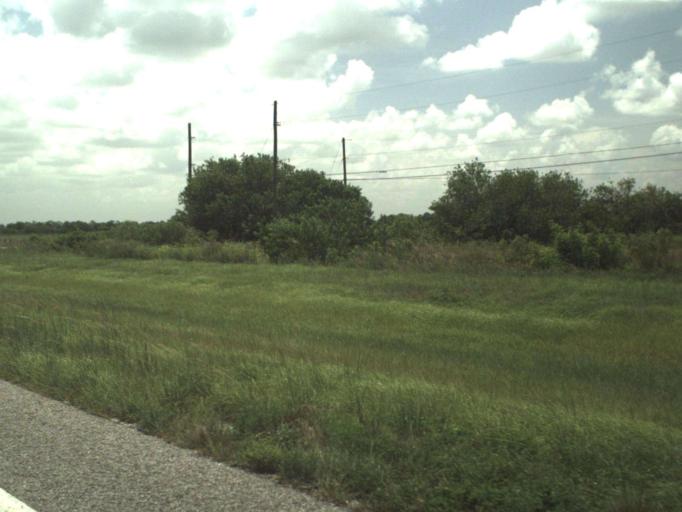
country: US
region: Florida
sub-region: Saint Lucie County
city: Fort Pierce South
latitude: 27.3670
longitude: -80.5377
